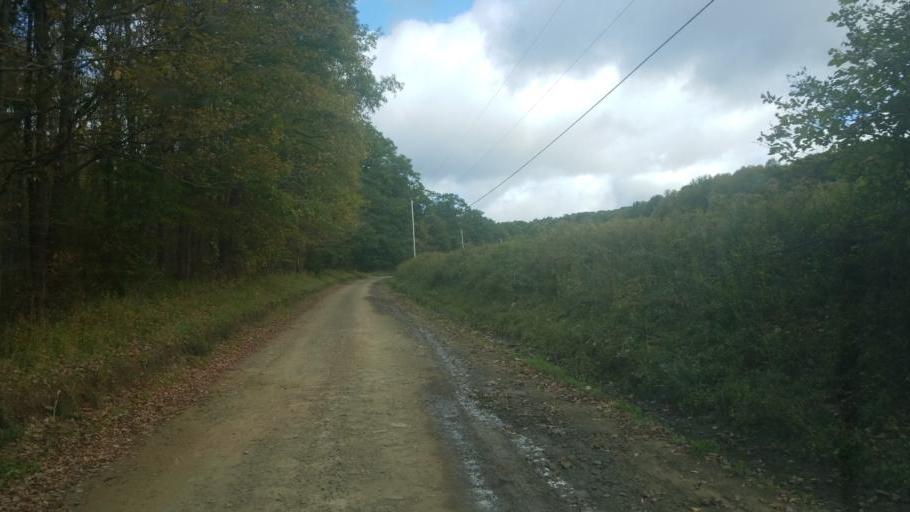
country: US
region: New York
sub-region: Allegany County
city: Cuba
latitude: 42.1366
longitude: -78.3020
